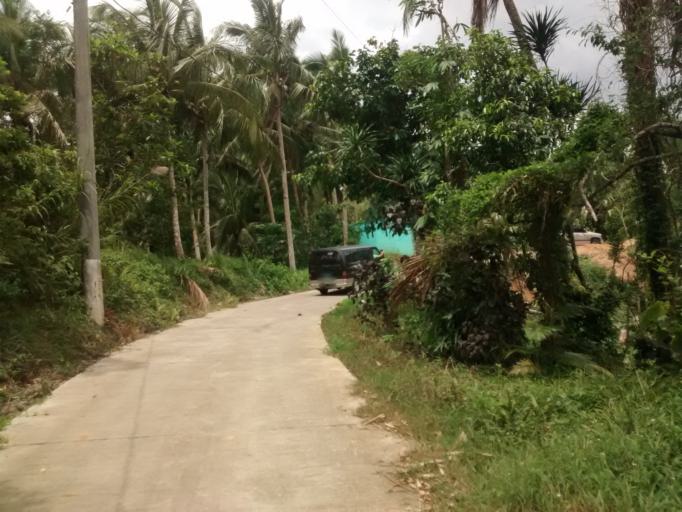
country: PH
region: Calabarzon
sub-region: Province of Quezon
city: Lucban
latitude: 14.1555
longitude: 121.5558
